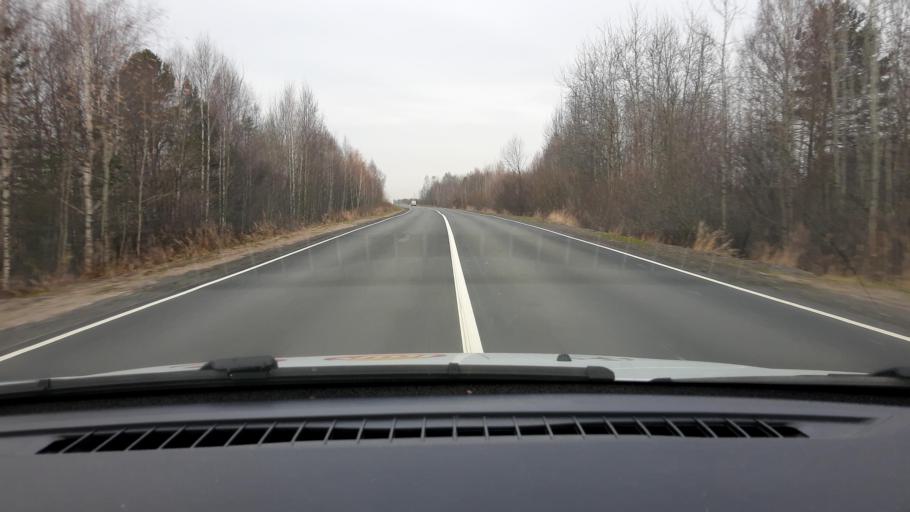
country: RU
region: Nizjnij Novgorod
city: Novaya Balakhna
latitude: 56.5741
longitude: 43.7035
